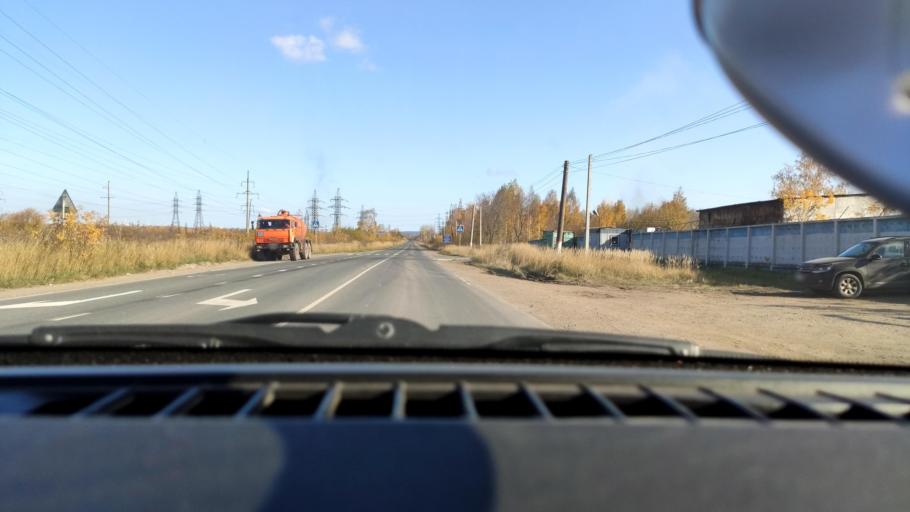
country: RU
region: Perm
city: Gamovo
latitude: 57.8869
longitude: 56.1673
